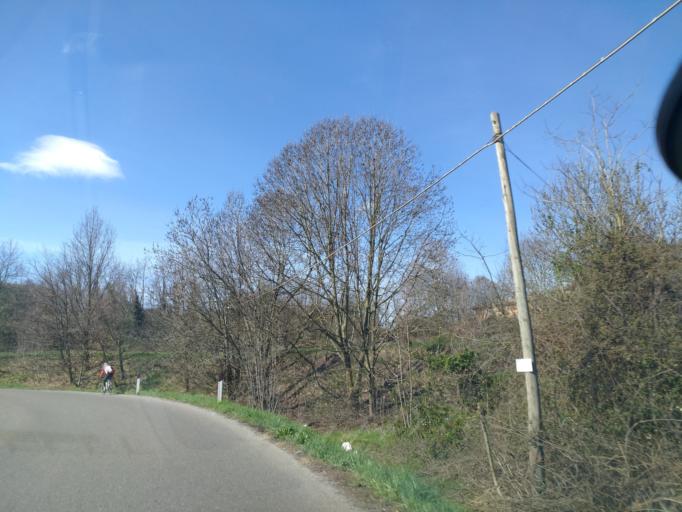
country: IT
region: Lombardy
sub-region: Provincia di Como
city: Anzano del Parco
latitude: 45.7613
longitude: 9.1991
